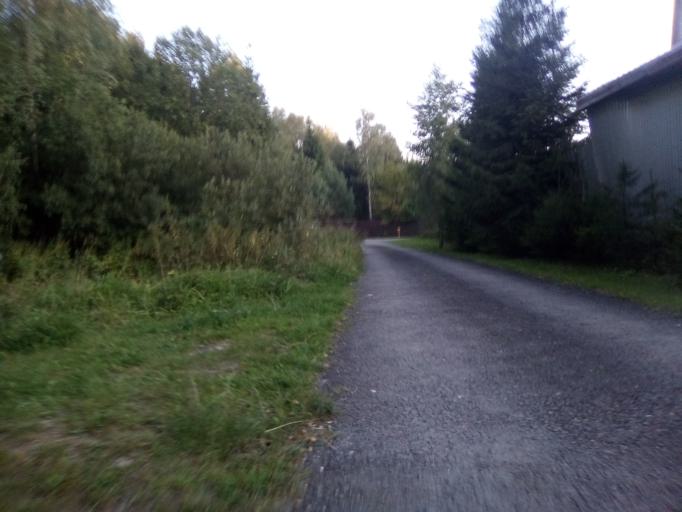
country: RU
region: Moskovskaya
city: Krasnoznamensk
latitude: 55.5652
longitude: 37.0296
